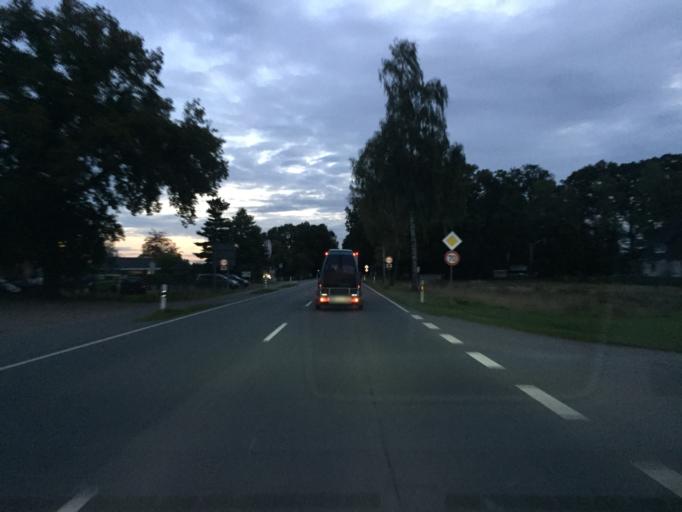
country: DE
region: Lower Saxony
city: Stuhr
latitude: 52.9804
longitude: 8.7451
